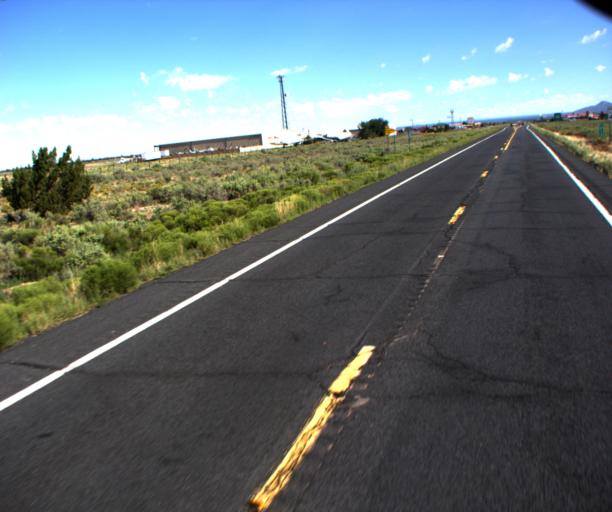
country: US
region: Arizona
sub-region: Coconino County
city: Williams
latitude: 35.6450
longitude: -112.1404
